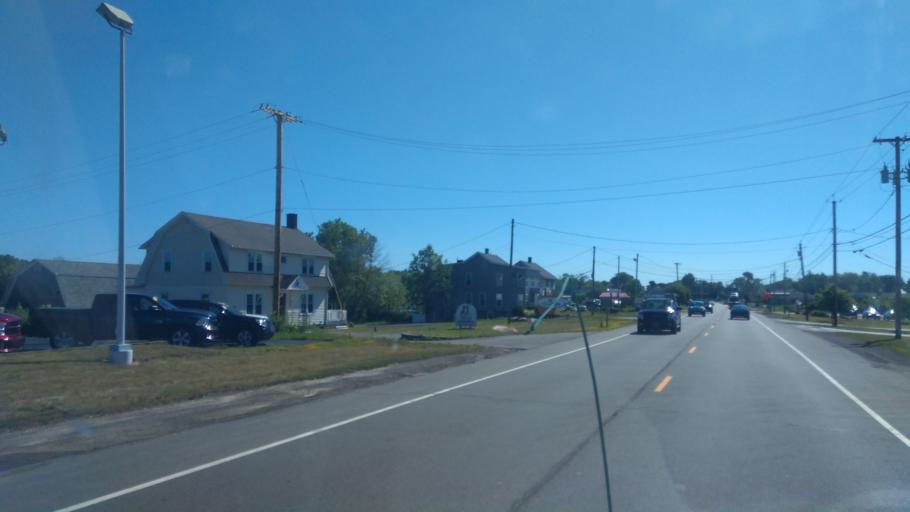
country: US
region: New York
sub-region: Monroe County
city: Webster
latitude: 43.2043
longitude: -77.4813
